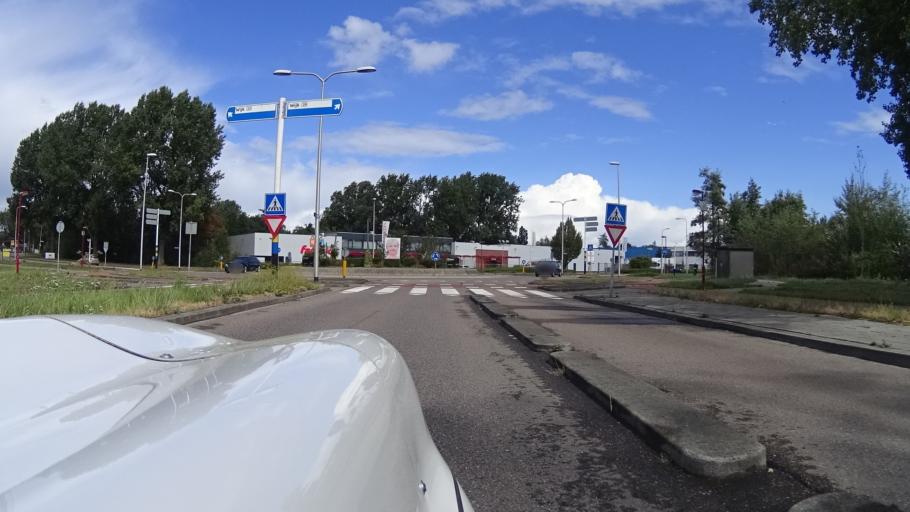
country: NL
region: South Holland
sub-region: Gemeente Zoetermeer
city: Zoetermeer
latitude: 52.0580
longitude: 4.5194
